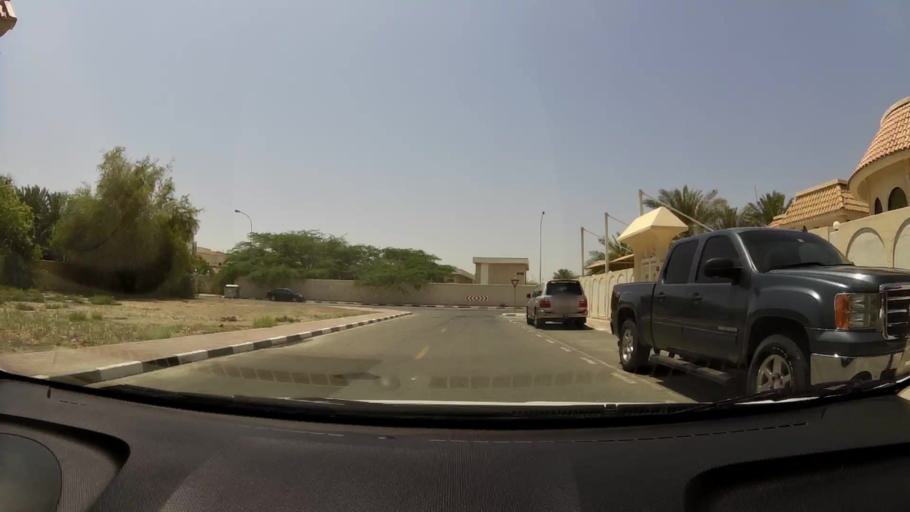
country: AE
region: Ash Shariqah
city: Sharjah
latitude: 25.2937
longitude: 55.3435
